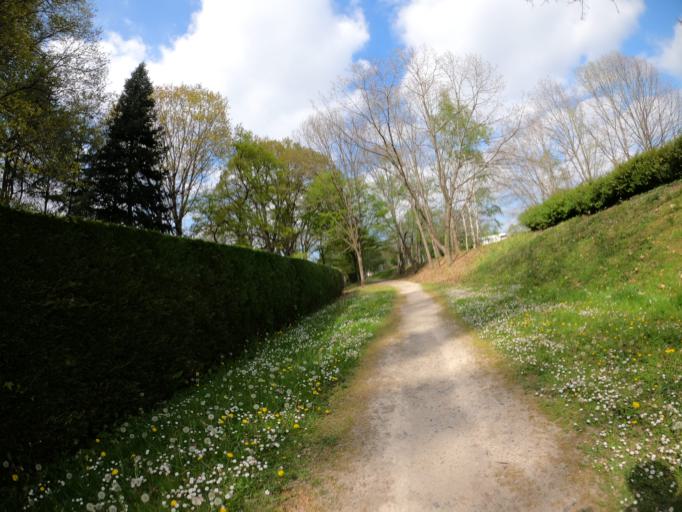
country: FR
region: Aquitaine
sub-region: Departement des Pyrenees-Atlantiques
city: Lons
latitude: 43.3340
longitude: -0.3846
